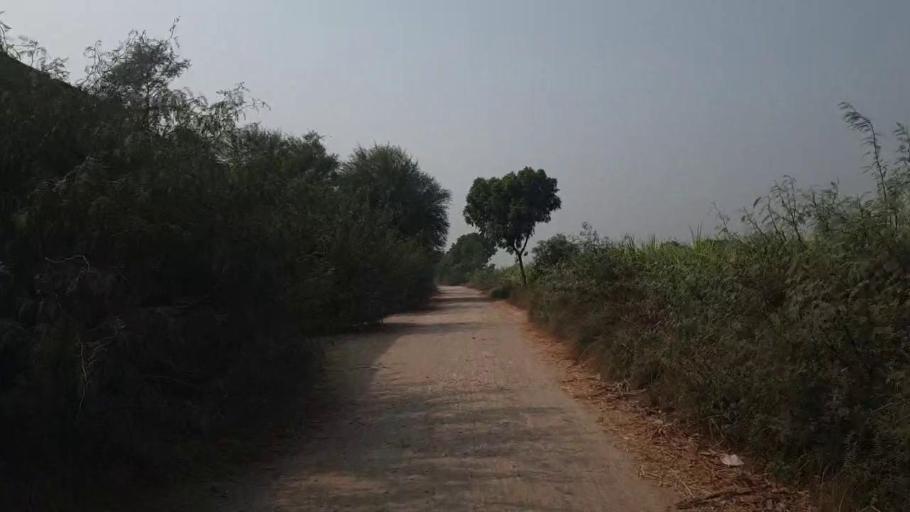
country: PK
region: Sindh
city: Tando Muhammad Khan
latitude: 25.2253
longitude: 68.5649
